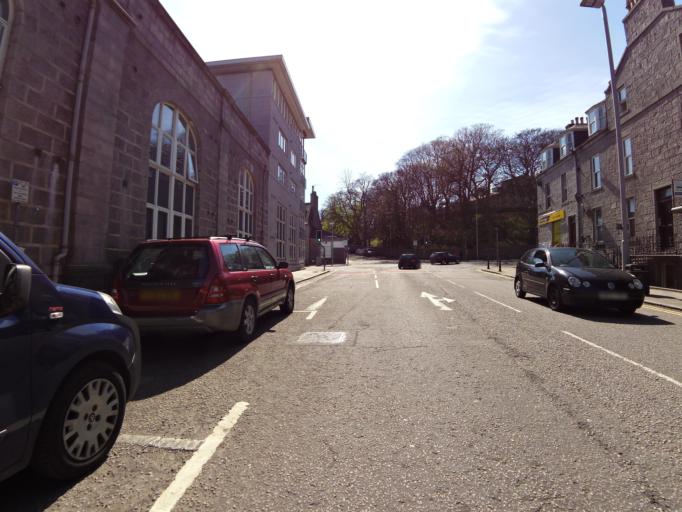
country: GB
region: Scotland
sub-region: Aberdeen City
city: Aberdeen
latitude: 57.1394
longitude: -2.1008
